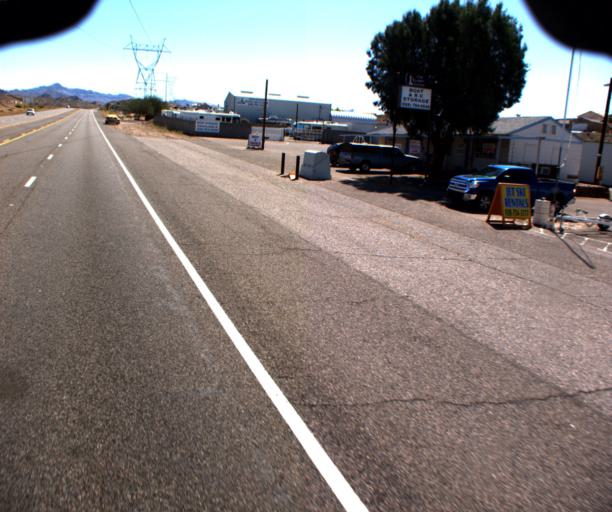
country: US
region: Nevada
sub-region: Clark County
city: Laughlin
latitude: 35.1900
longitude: -114.5346
